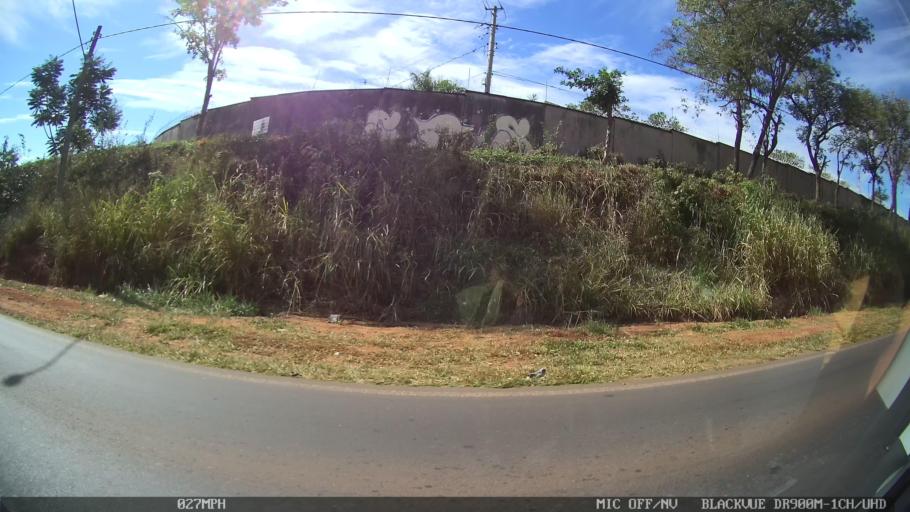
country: BR
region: Sao Paulo
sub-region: Sao Jose Do Rio Preto
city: Sao Jose do Rio Preto
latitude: -20.8294
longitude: -49.3424
